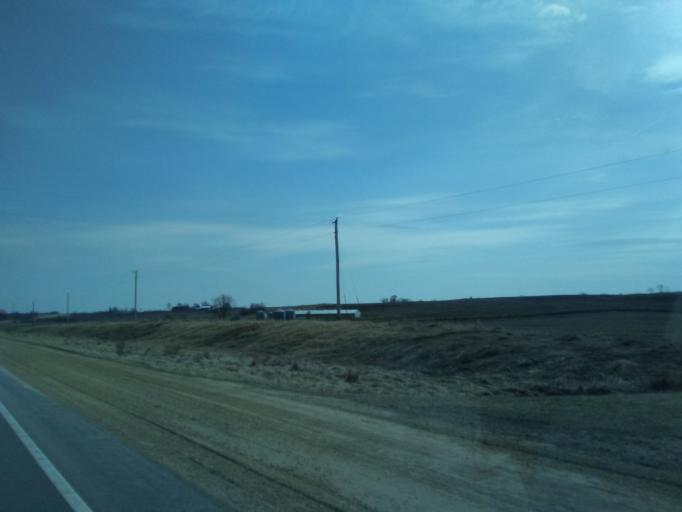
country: US
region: Iowa
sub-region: Winneshiek County
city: Decorah
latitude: 43.3990
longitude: -91.8423
